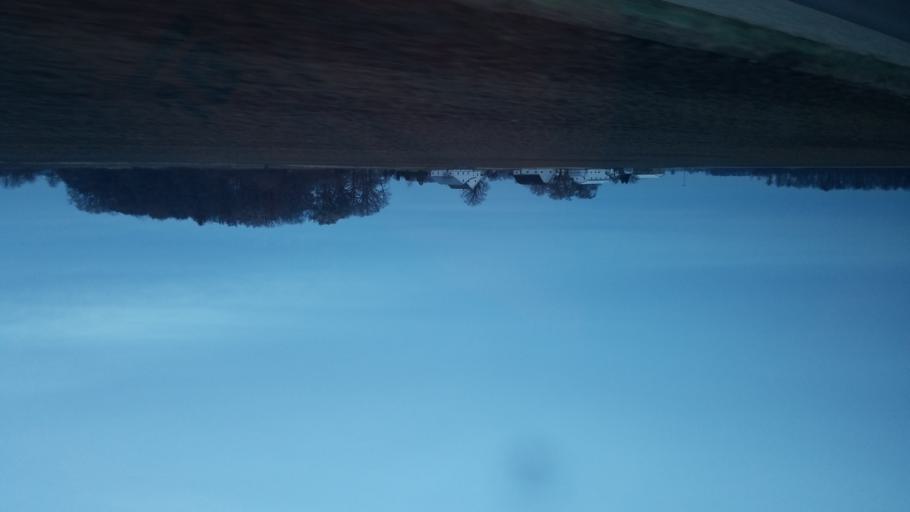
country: US
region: Indiana
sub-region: Adams County
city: Berne
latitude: 40.7416
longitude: -84.9948
